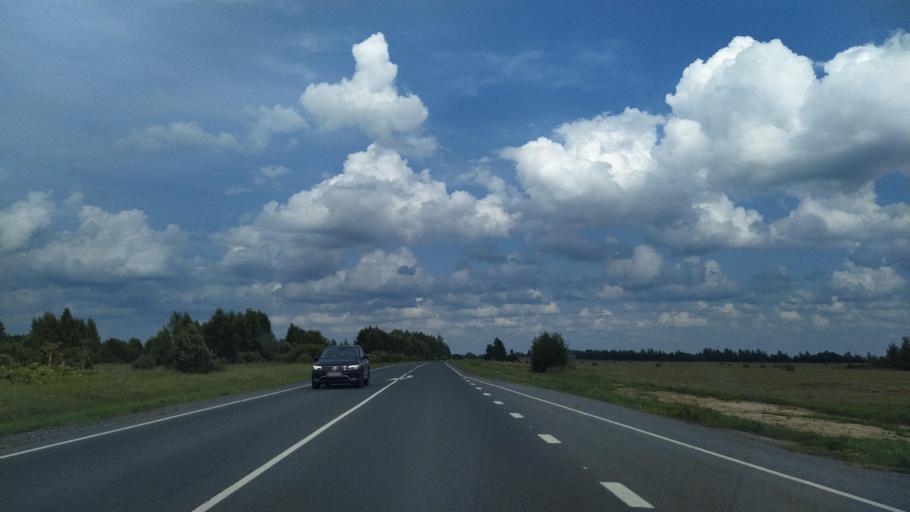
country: RU
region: Novgorod
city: Sol'tsy
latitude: 58.0775
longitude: 30.0720
